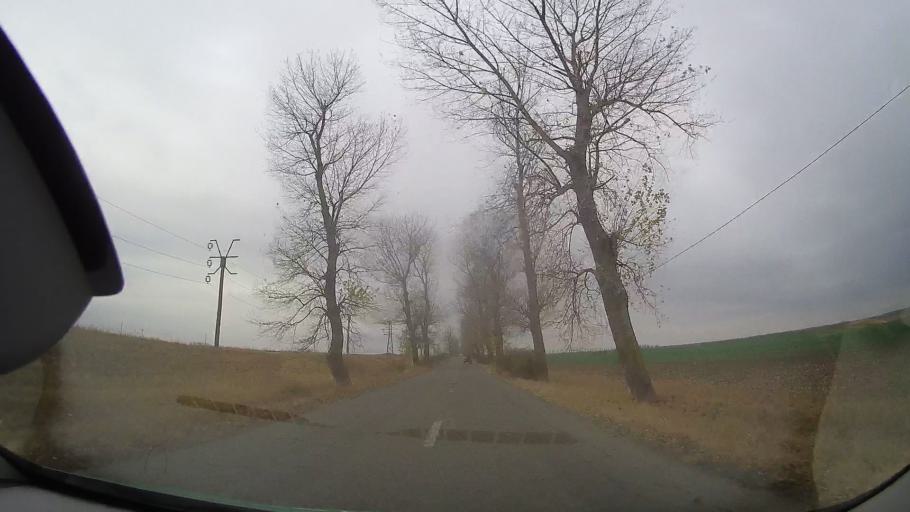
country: RO
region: Braila
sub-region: Comuna Ulmu
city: Jugureanu
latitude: 44.9419
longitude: 27.2585
